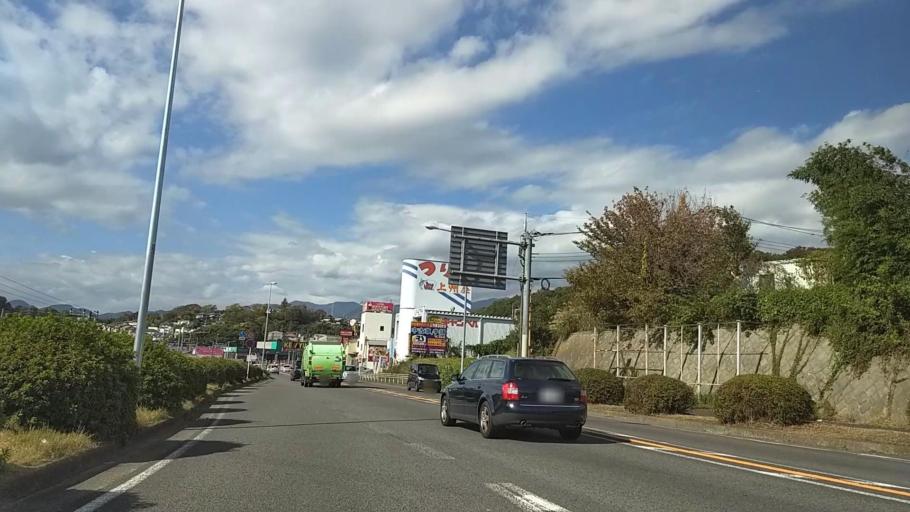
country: JP
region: Kanagawa
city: Hadano
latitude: 35.3804
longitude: 139.2320
